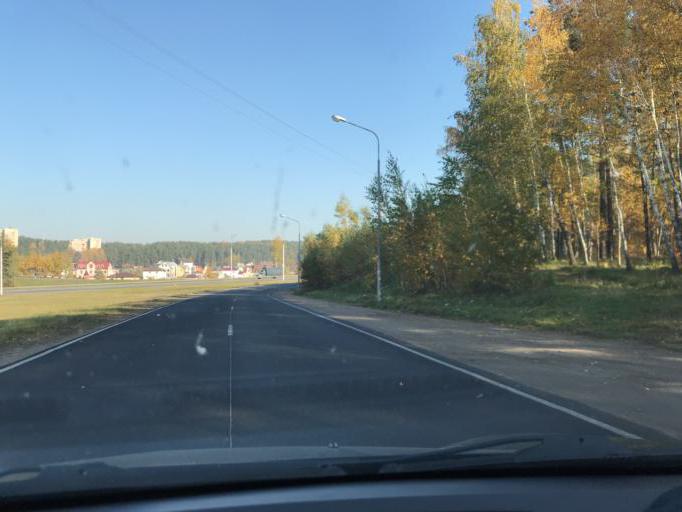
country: BY
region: Minsk
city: Pryvol'ny
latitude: 53.8208
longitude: 27.7579
